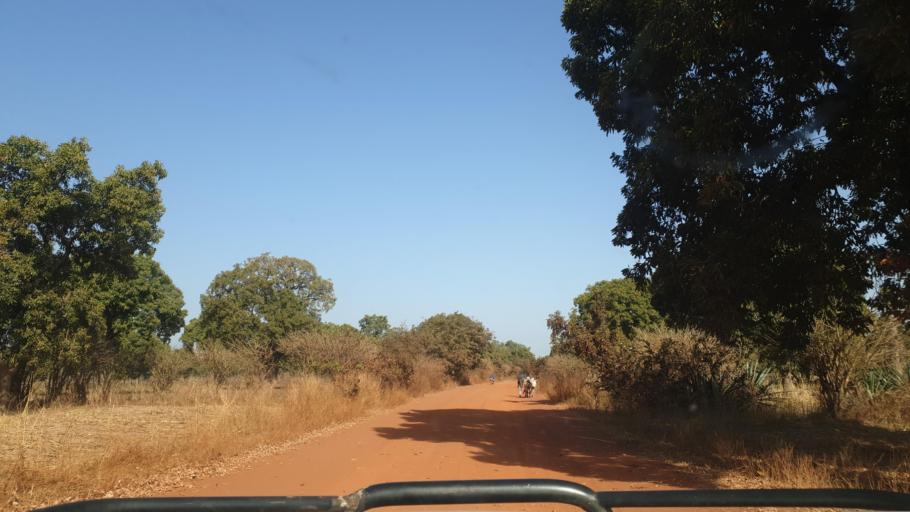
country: ML
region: Sikasso
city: Kolondieba
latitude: 11.7369
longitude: -6.8938
